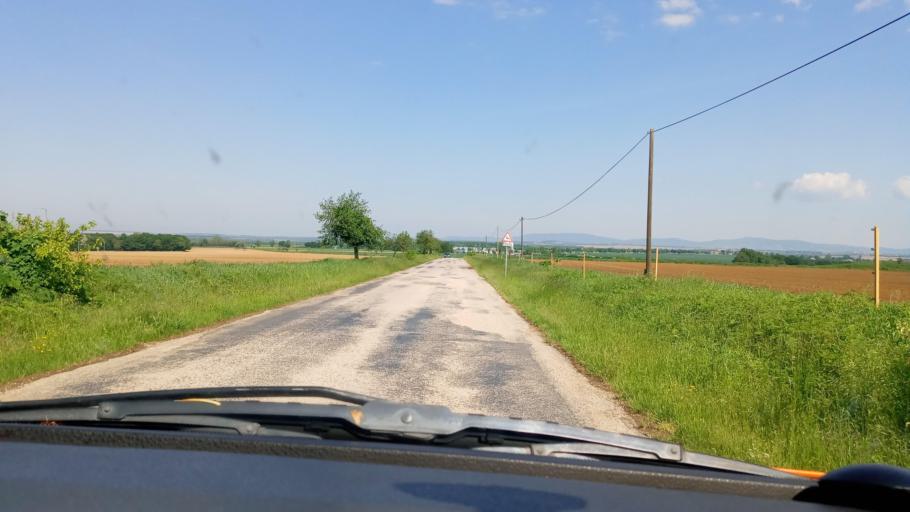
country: HU
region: Baranya
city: Harkany
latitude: 45.9105
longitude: 18.2444
